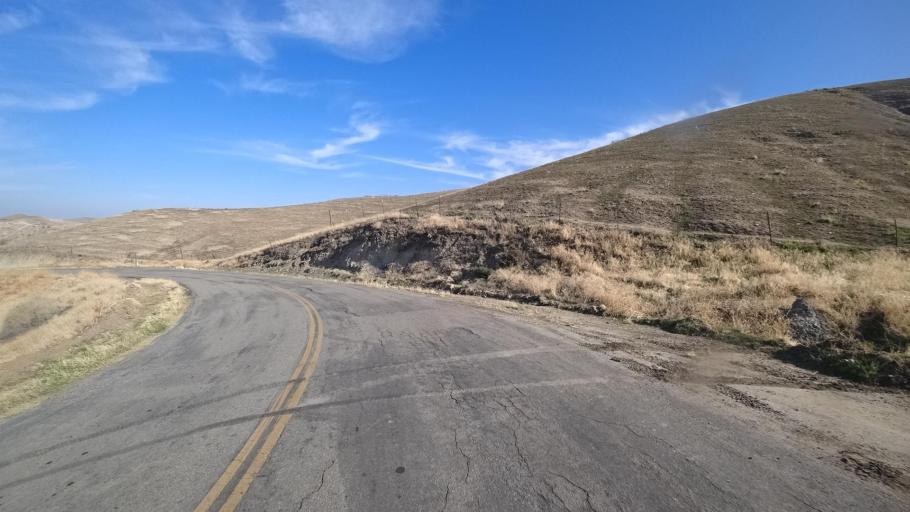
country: US
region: California
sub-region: Kern County
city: Lamont
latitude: 35.3886
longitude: -118.8171
